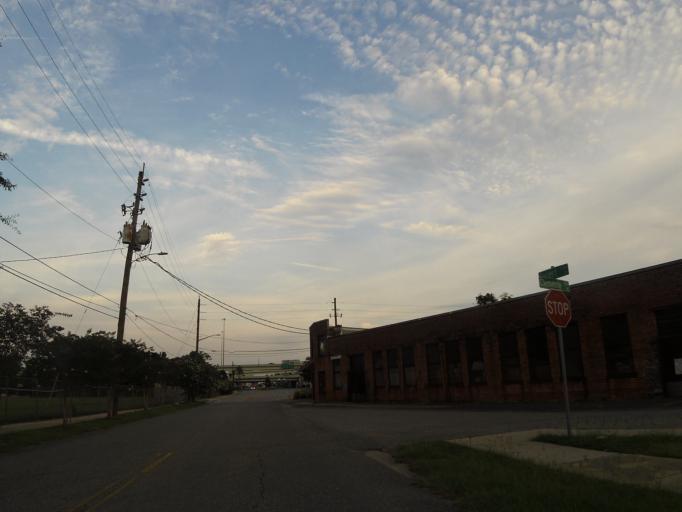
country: US
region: Florida
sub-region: Duval County
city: Jacksonville
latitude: 30.3249
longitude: -81.6843
